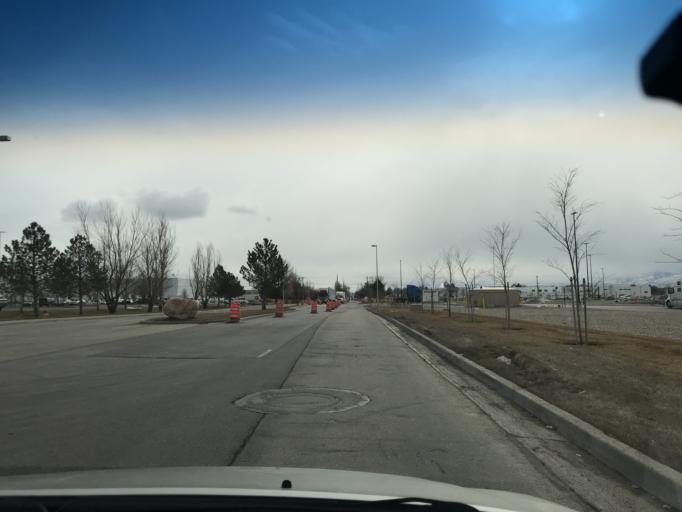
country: US
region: Utah
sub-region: Salt Lake County
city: West Valley City
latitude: 40.7863
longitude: -112.0252
